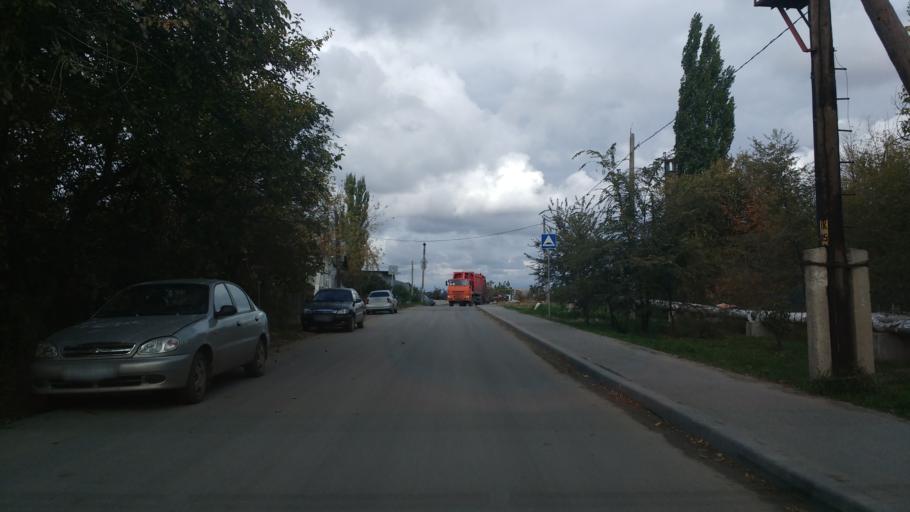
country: RU
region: Volgograd
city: Vodstroy
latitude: 48.7769
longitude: 44.5421
